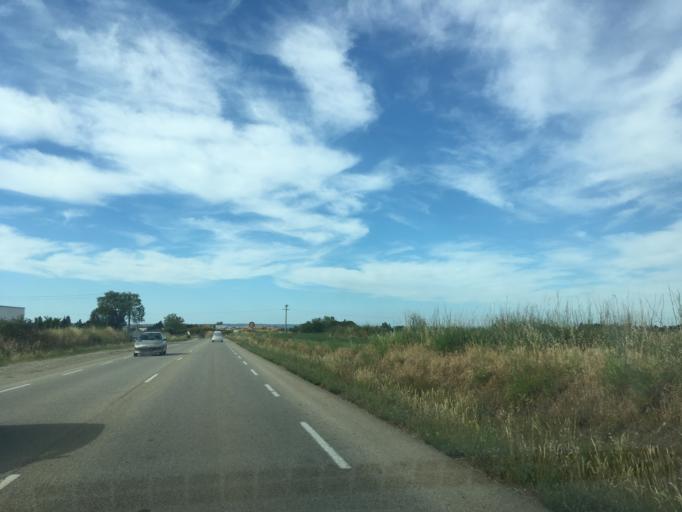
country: FR
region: Languedoc-Roussillon
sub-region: Departement du Gard
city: Garons
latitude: 43.7796
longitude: 4.4298
